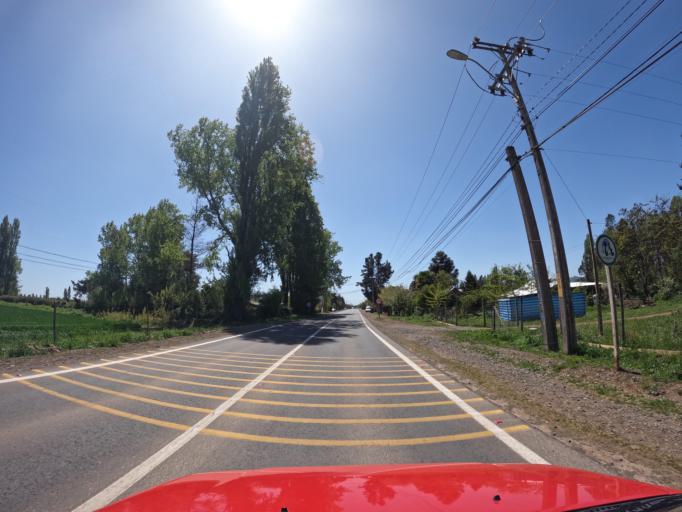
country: CL
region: Maule
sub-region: Provincia de Linares
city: Colbun
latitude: -35.7421
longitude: -71.4222
